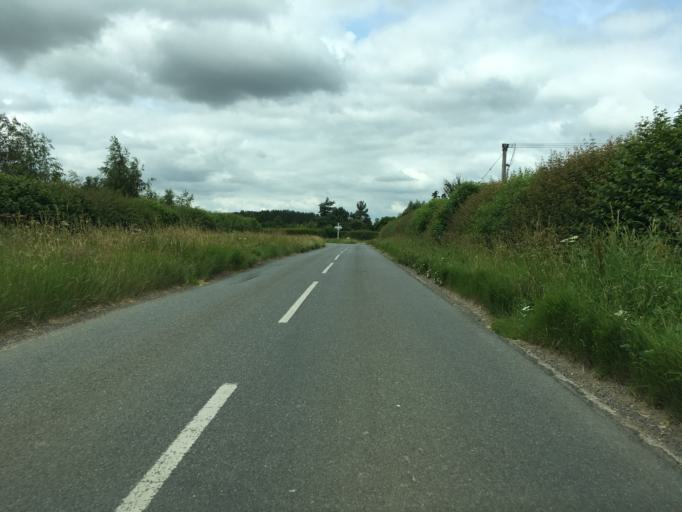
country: GB
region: England
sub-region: Oxfordshire
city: Shipton under Wychwood
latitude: 51.9029
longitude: -1.6210
